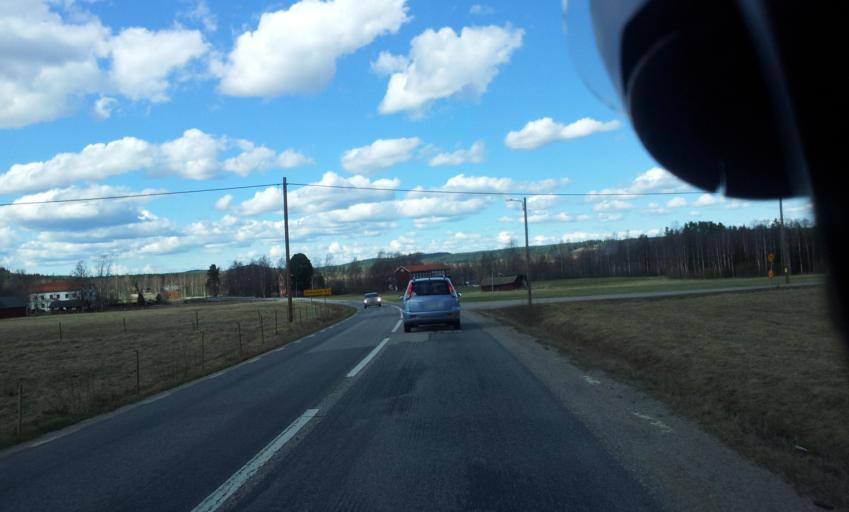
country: SE
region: Gaevleborg
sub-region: Ovanakers Kommun
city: Edsbyn
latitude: 61.3080
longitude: 15.8854
